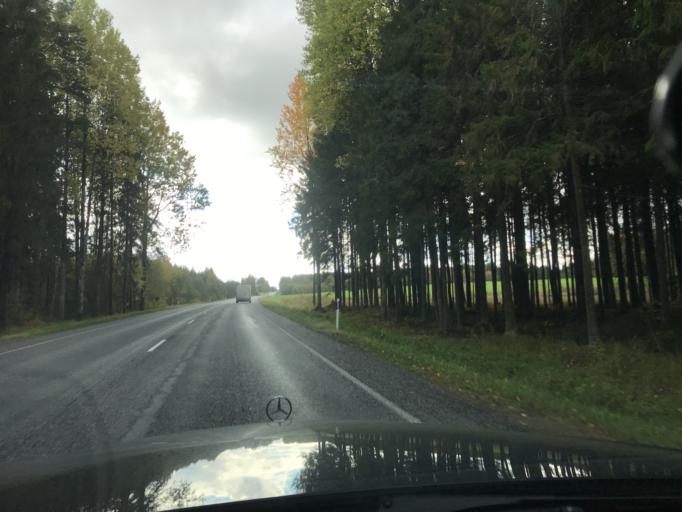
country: RU
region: Pskov
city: Pechory
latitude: 57.7209
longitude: 27.3164
